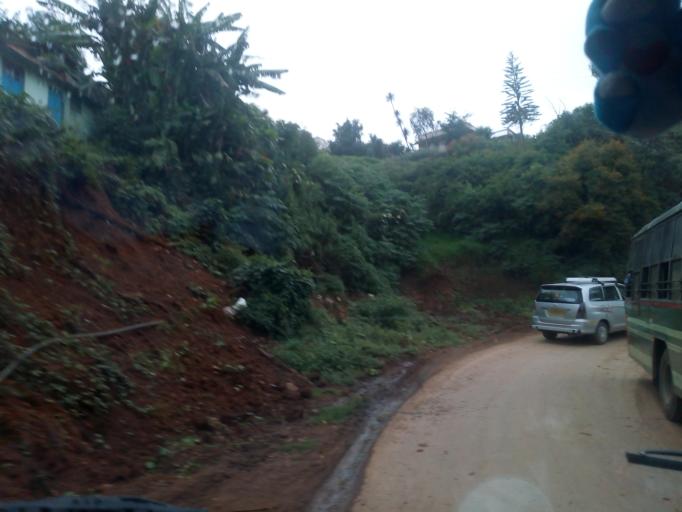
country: IN
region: Tamil Nadu
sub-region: Nilgiri
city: Ooty
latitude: 11.3943
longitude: 76.7179
